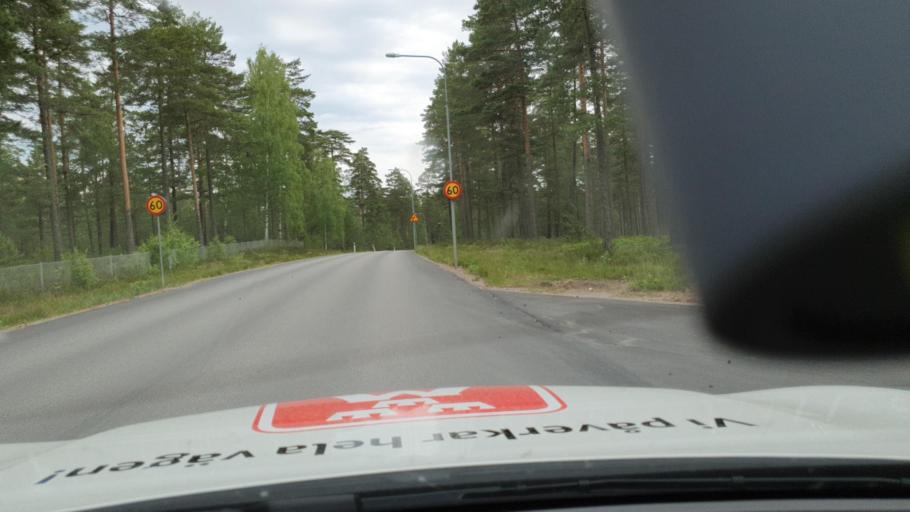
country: SE
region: Vaestra Goetaland
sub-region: Karlsborgs Kommun
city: Karlsborg
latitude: 58.5512
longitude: 14.4787
